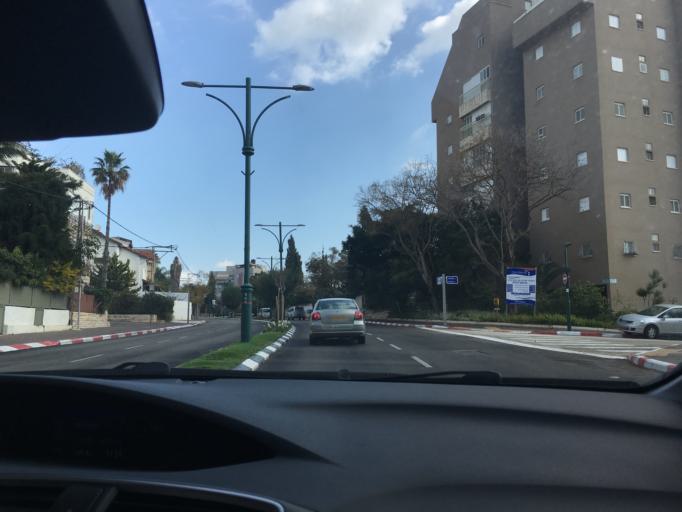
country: IL
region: Tel Aviv
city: Ramat HaSharon
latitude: 32.1596
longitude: 34.8470
